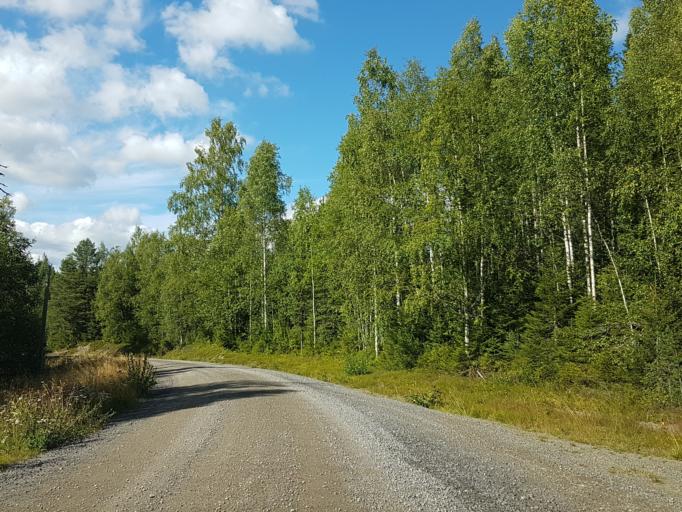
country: SE
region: Vaesterbotten
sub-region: Skelleftea Kommun
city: Burtraesk
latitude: 64.2778
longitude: 20.4798
